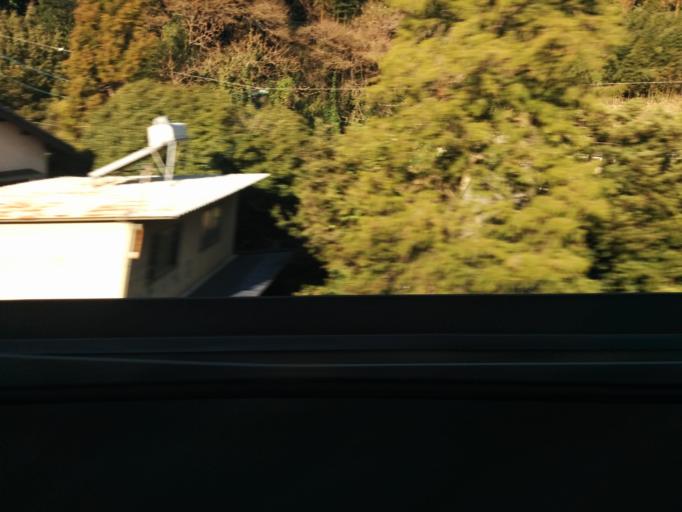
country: JP
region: Shizuoka
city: Shizuoka-shi
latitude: 34.9223
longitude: 138.3592
